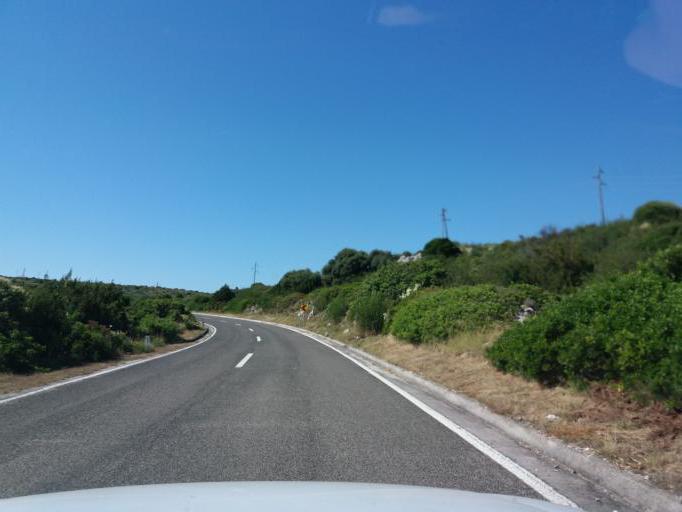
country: HR
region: Zadarska
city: Ugljan
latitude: 44.0229
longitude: 15.0356
